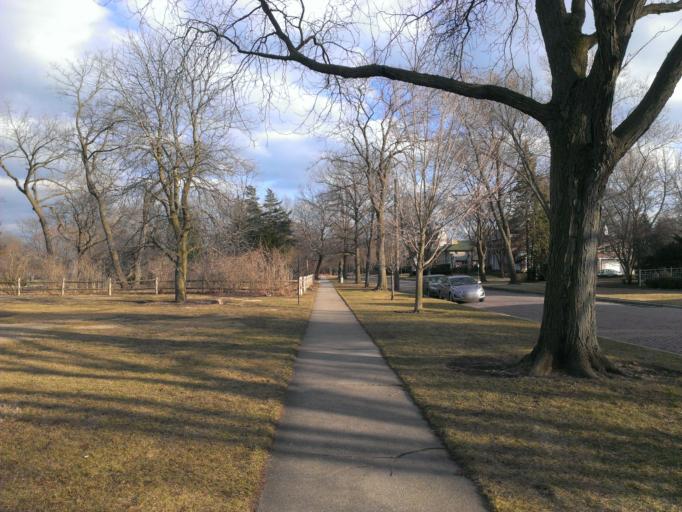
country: US
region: Illinois
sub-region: Cook County
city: Kenilworth
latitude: 42.0790
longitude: -87.6890
